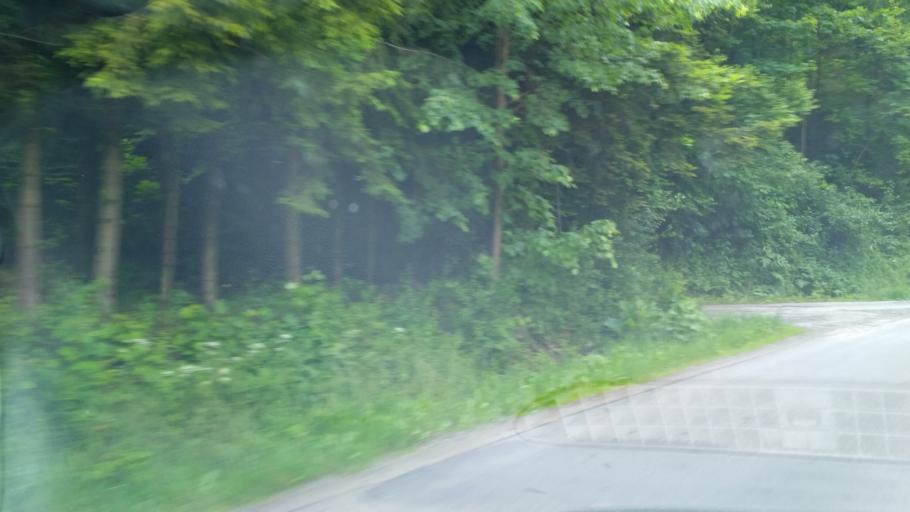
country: PL
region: Subcarpathian Voivodeship
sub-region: Powiat przemyski
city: Dubiecko
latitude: 49.8366
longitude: 22.3971
